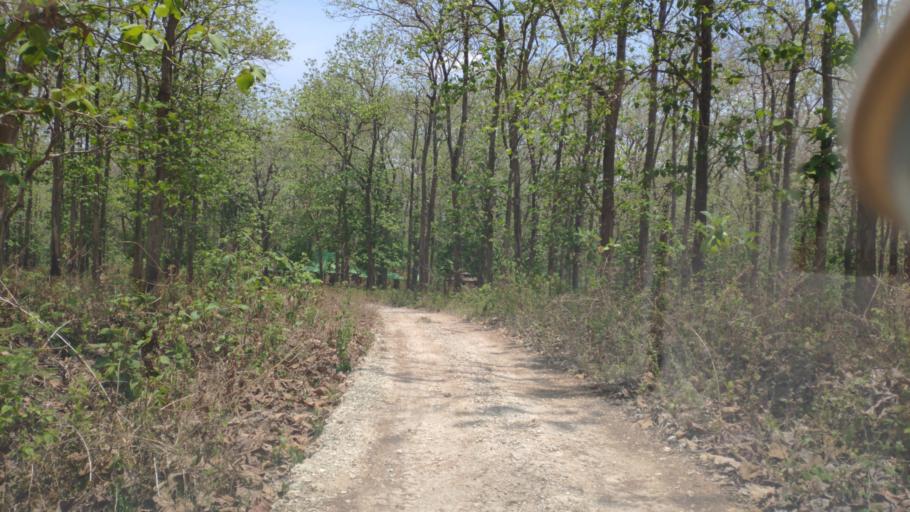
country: ID
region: Central Java
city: Botoh
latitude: -7.0745
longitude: 111.4835
